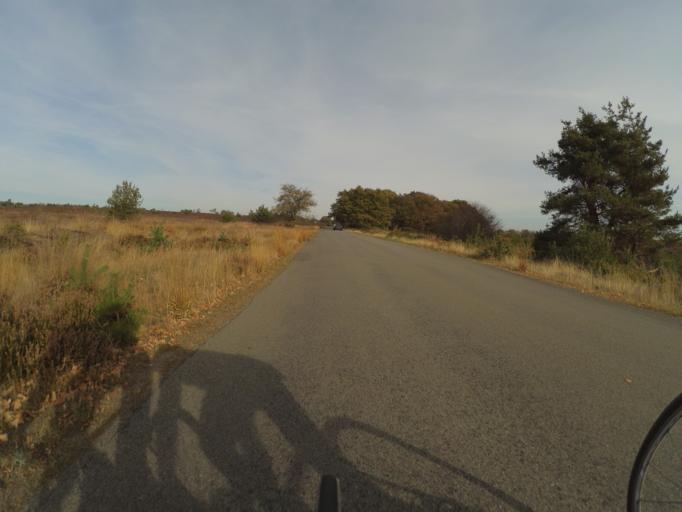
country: NL
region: Overijssel
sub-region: Gemeente Hof van Twente
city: Markelo
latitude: 52.3427
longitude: 6.4265
